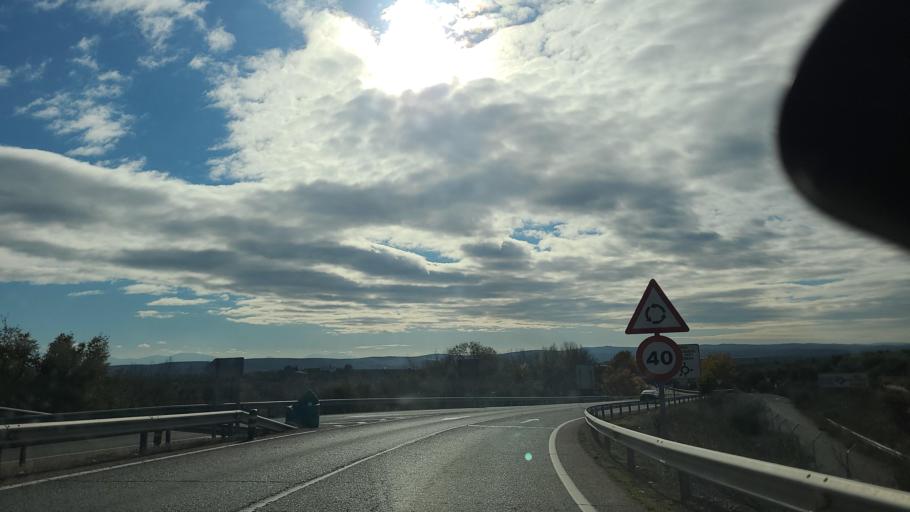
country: ES
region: Andalusia
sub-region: Provincia de Jaen
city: Villanueva de la Reina
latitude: 38.0476
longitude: -3.9084
